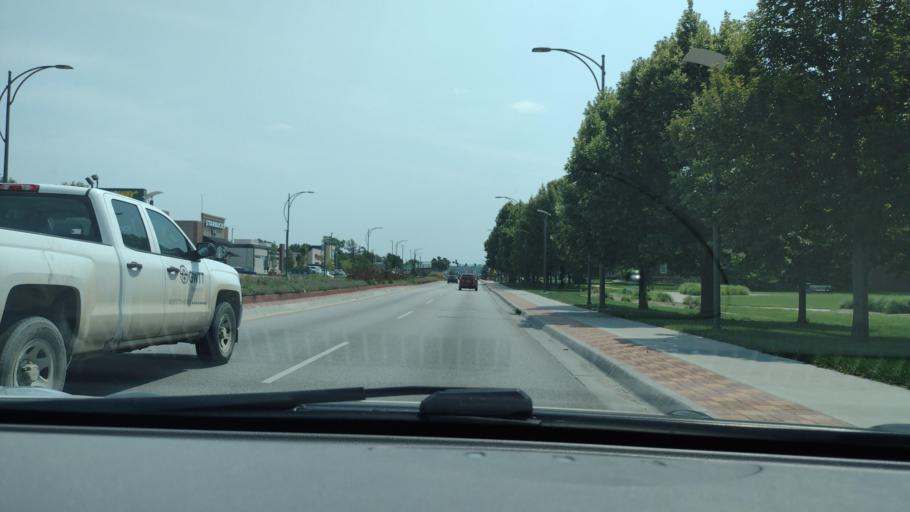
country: US
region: Iowa
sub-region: Pottawattamie County
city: Council Bluffs
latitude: 41.2620
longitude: -95.8851
